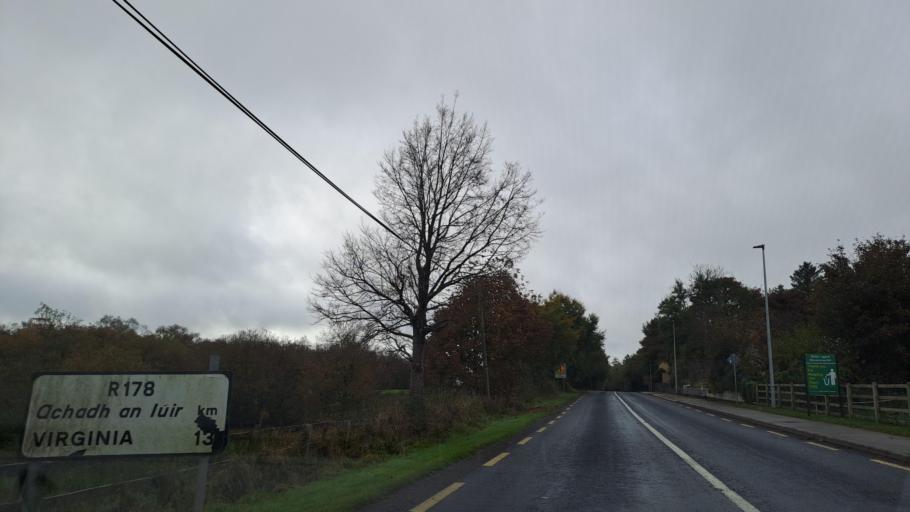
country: IE
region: Ulster
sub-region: An Cabhan
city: Bailieborough
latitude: 53.9100
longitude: -6.9755
